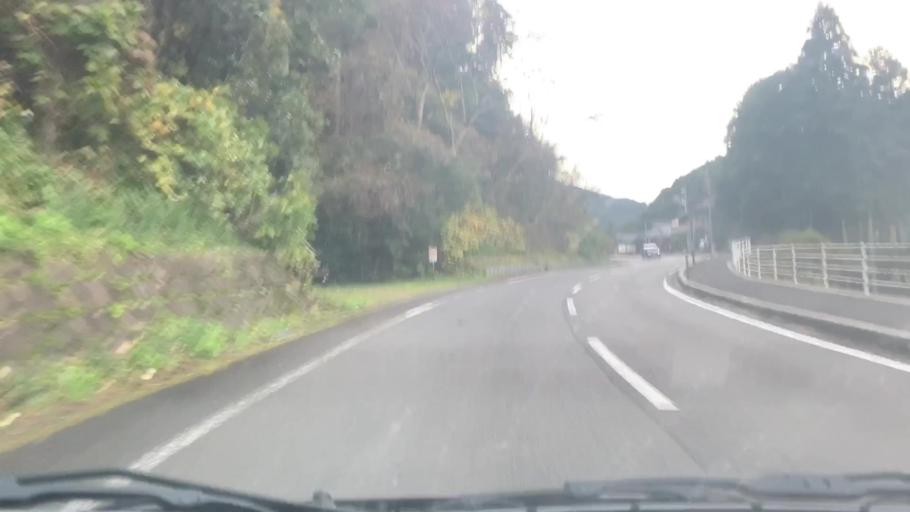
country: JP
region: Saga Prefecture
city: Kashima
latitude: 33.0220
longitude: 130.0672
